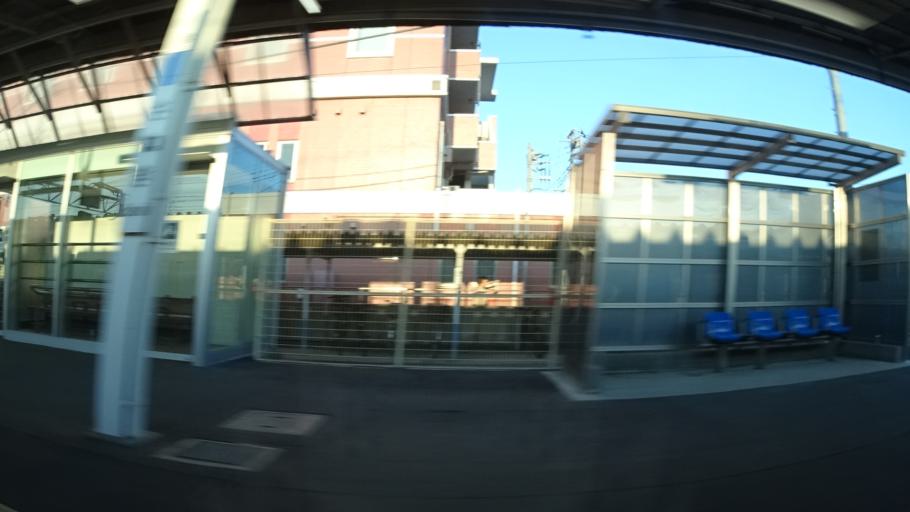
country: JP
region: Ibaraki
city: Fujishiro
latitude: 35.9296
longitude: 140.1382
